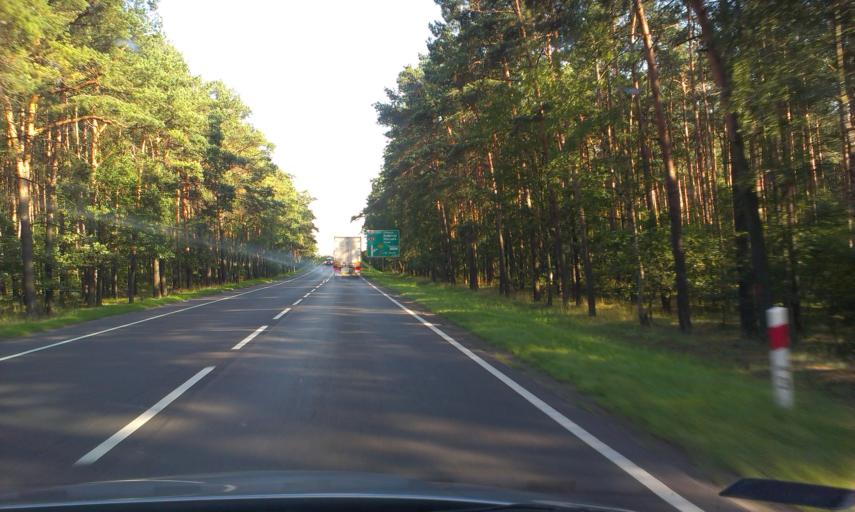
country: PL
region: Kujawsko-Pomorskie
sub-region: Powiat bydgoski
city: Biale Blota
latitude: 53.1034
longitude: 17.8887
